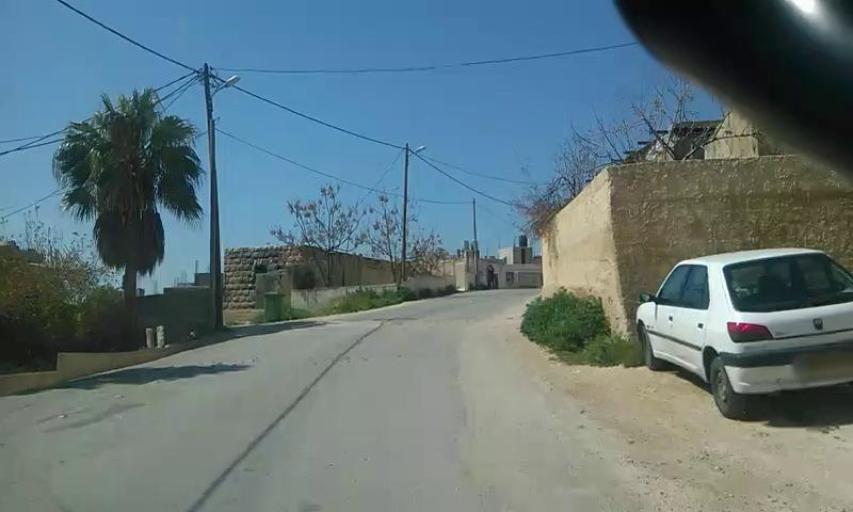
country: PS
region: West Bank
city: Al Majd
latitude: 31.4798
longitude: 34.9514
